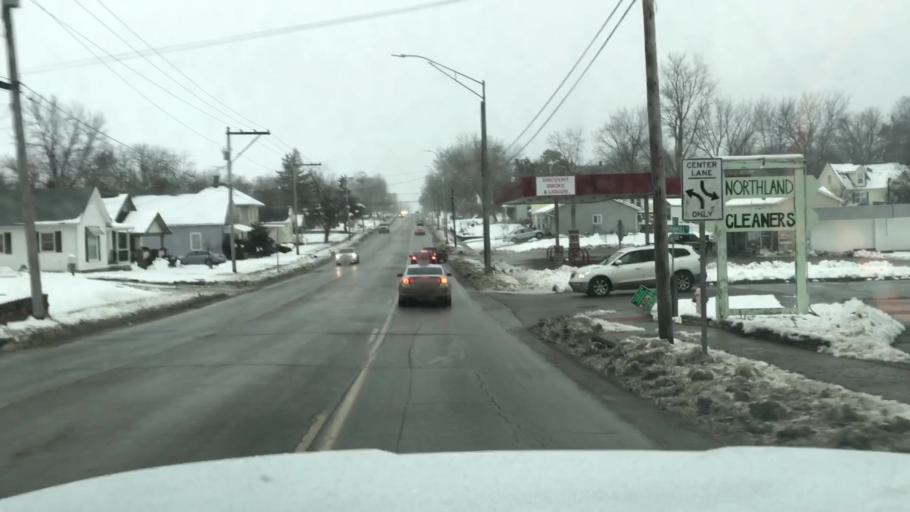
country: US
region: Missouri
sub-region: Clinton County
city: Cameron
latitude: 39.7377
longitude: -94.2360
